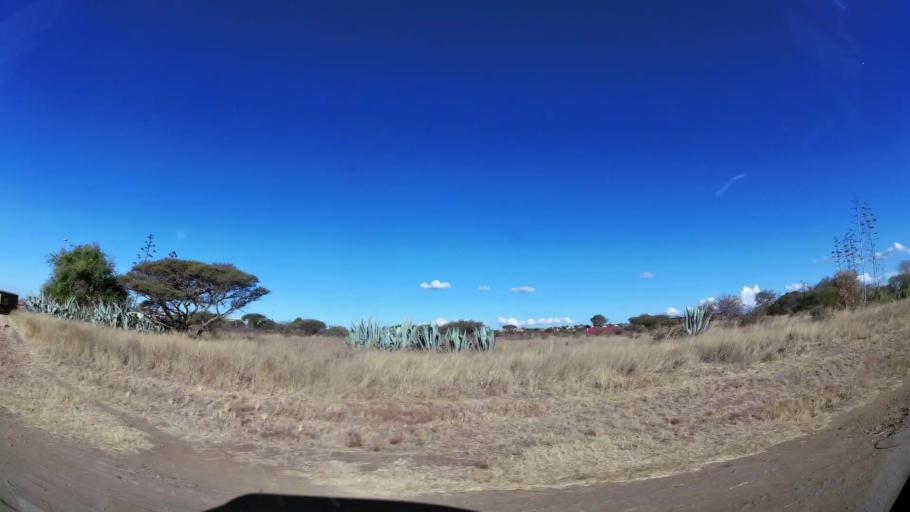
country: ZA
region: Limpopo
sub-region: Capricorn District Municipality
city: Polokwane
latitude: -23.8744
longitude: 29.4803
